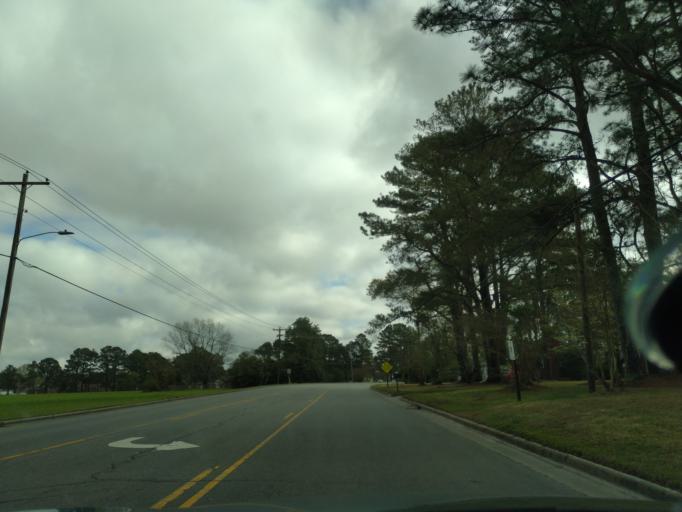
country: US
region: North Carolina
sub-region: Chowan County
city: Edenton
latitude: 36.0606
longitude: -76.6223
